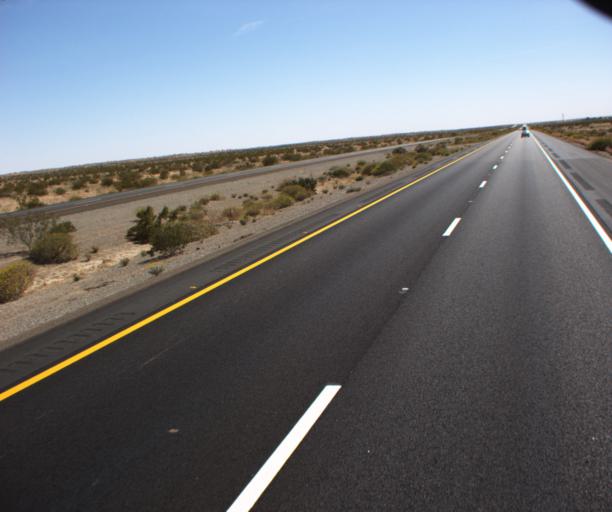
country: US
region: Arizona
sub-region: Yuma County
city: Fortuna Foothills
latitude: 32.5843
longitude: -114.5511
